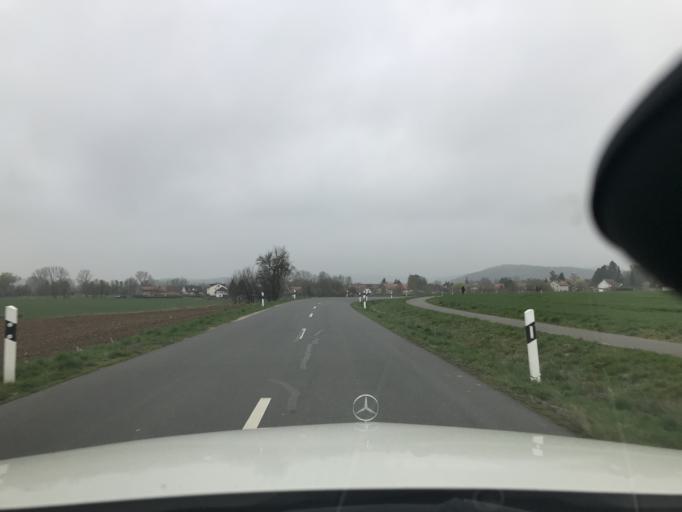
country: DE
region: Lower Saxony
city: Gemeinde Friedland
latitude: 51.4499
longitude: 9.9107
